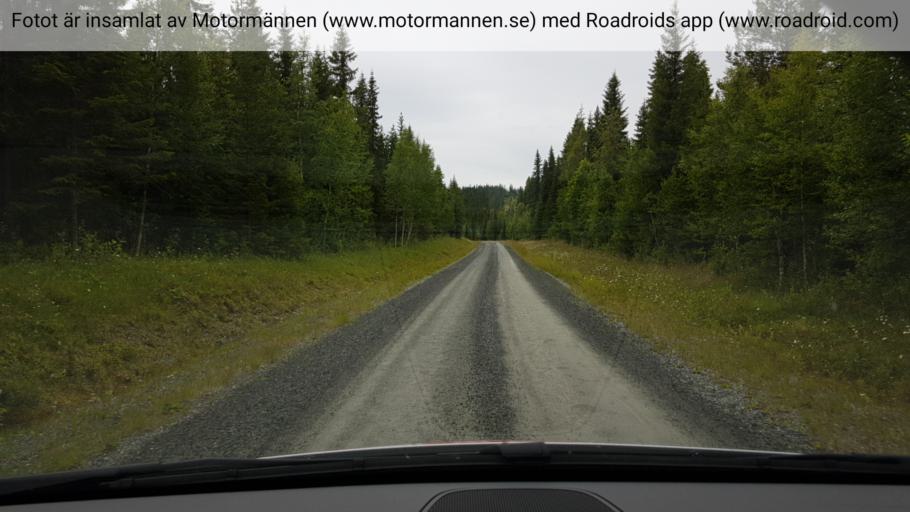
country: SE
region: Jaemtland
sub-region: Krokoms Kommun
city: Valla
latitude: 63.5821
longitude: 13.9549
